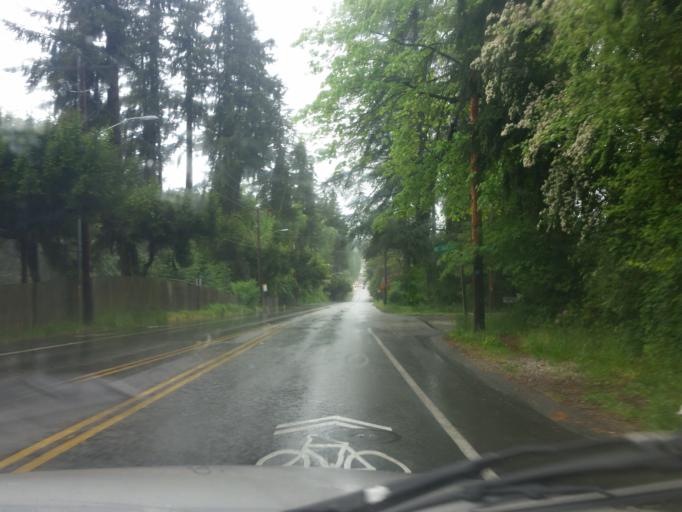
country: US
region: Washington
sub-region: King County
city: Kenmore
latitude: 47.7462
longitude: -122.2500
